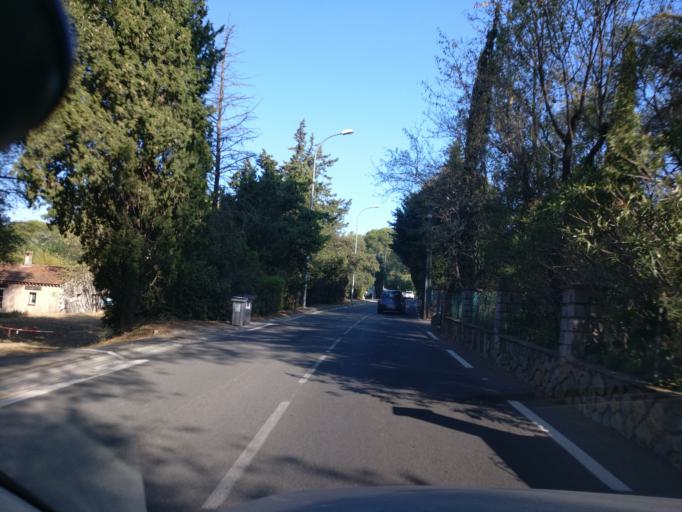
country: FR
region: Provence-Alpes-Cote d'Azur
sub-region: Departement du Var
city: Sanary-sur-Mer
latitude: 43.1351
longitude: 5.8129
